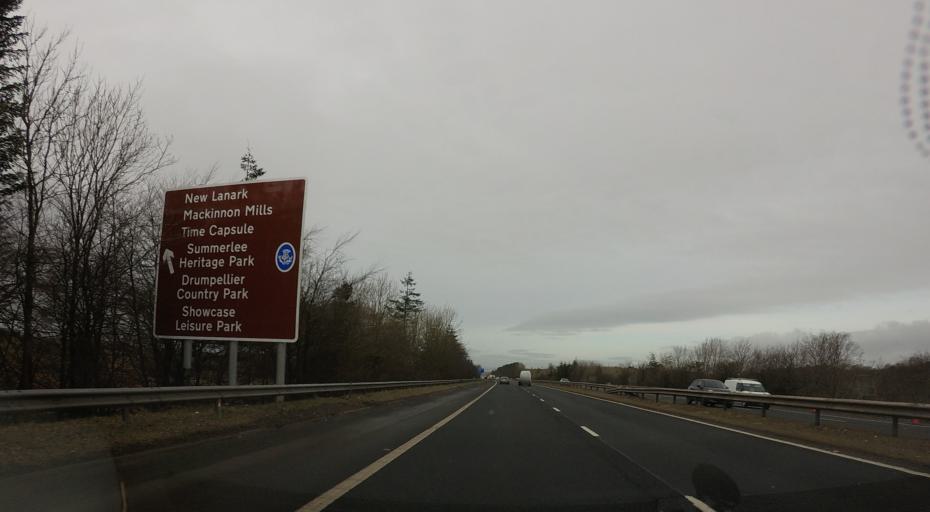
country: GB
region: Scotland
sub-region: North Lanarkshire
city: Caldercruix
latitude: 55.8440
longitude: -3.8928
